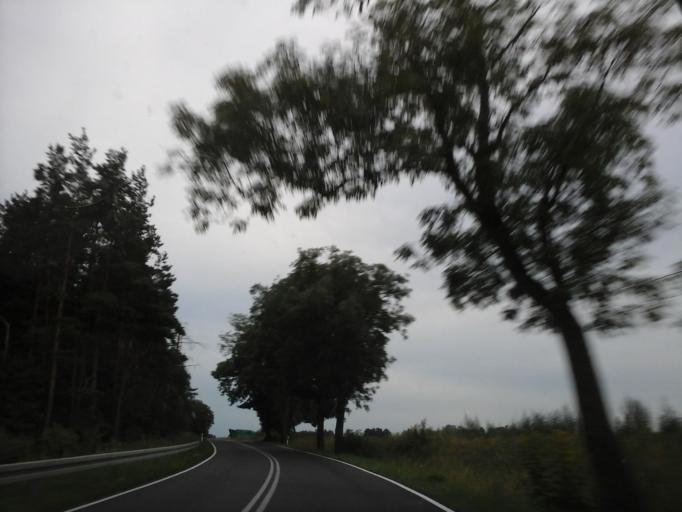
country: PL
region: West Pomeranian Voivodeship
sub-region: Powiat goleniowski
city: Maszewo
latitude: 53.4796
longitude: 15.0591
